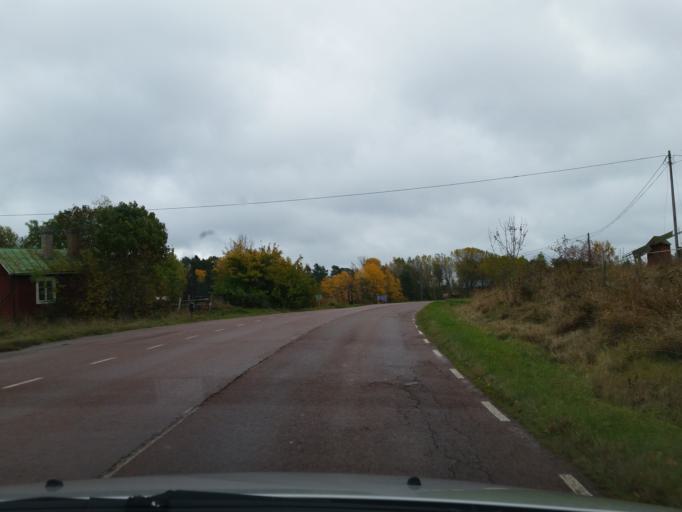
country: AX
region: Alands landsbygd
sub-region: Lumparland
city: Lumparland
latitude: 60.1158
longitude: 20.2611
